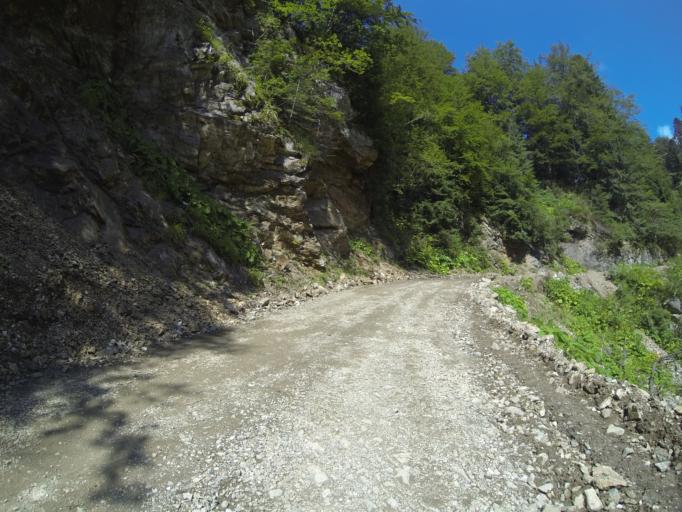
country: RO
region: Valcea
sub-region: Comuna Costesti
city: Bistrita
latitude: 45.2591
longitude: 23.9878
